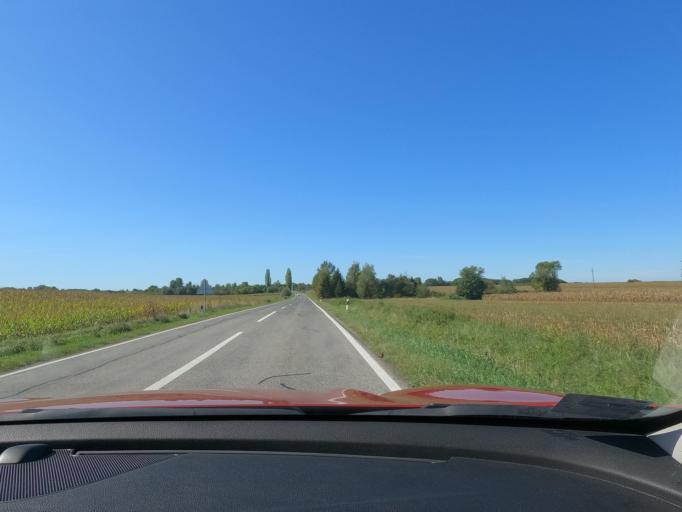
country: HR
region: Sisacko-Moslavacka
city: Osekovo
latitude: 45.5420
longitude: 16.5750
